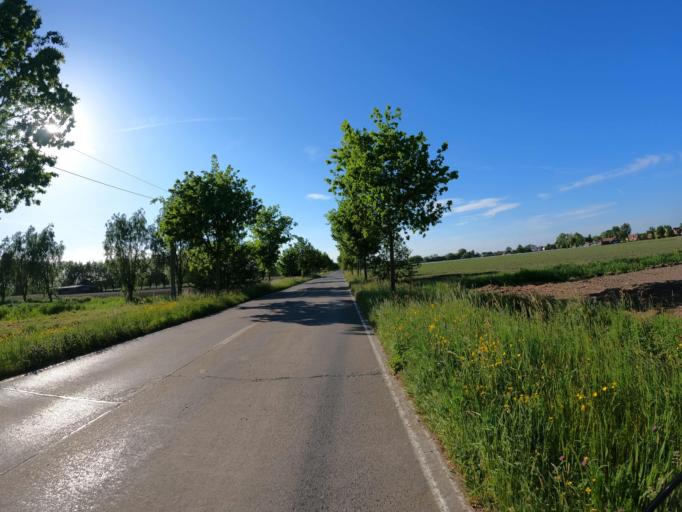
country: BE
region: Flanders
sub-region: Provincie Oost-Vlaanderen
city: Nazareth
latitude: 50.9725
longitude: 3.5743
